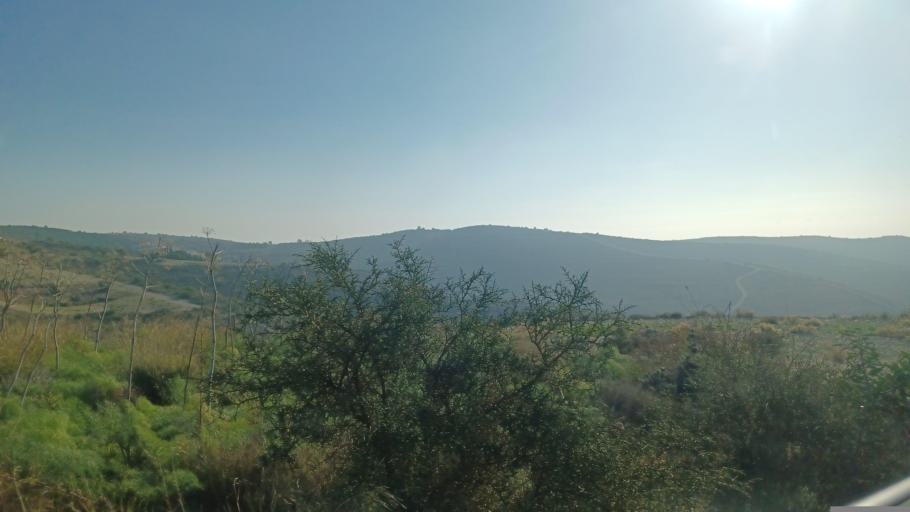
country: CY
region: Larnaka
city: Kofinou
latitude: 34.8434
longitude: 33.3015
